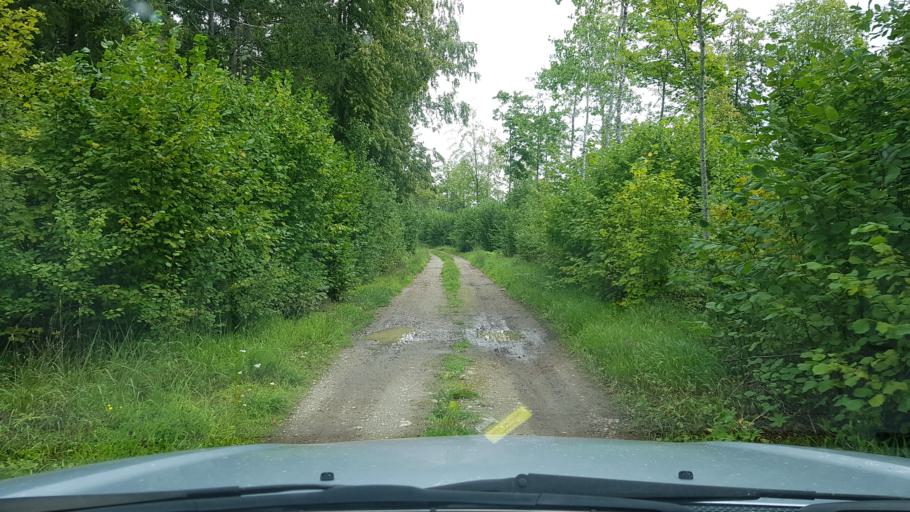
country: EE
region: Harju
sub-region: Rae vald
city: Vaida
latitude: 59.2725
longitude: 25.0208
